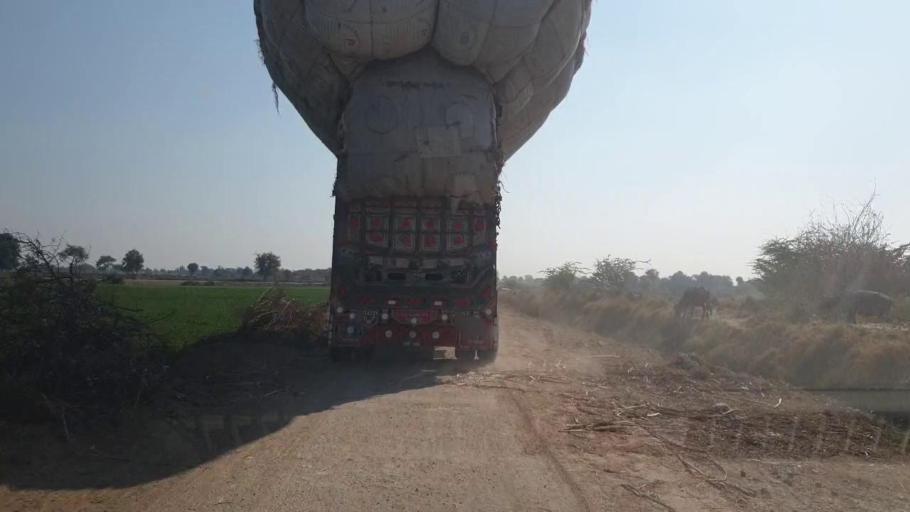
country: PK
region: Sindh
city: Shahdadpur
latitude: 25.9674
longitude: 68.6172
